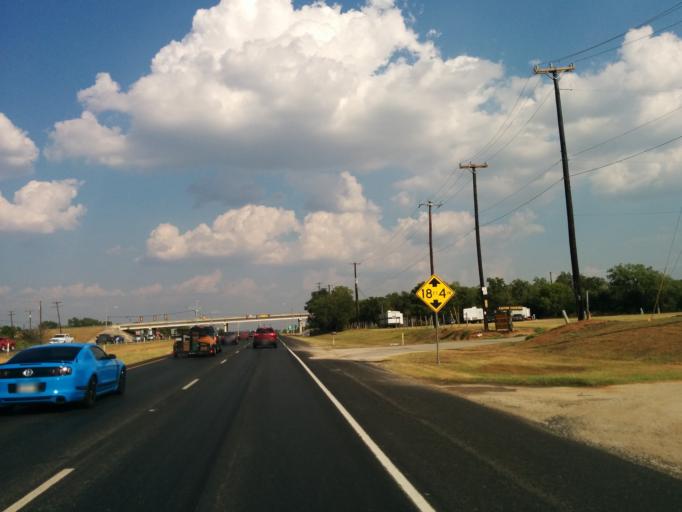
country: US
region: Texas
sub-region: Bexar County
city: Elmendorf
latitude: 29.2684
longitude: -98.3087
